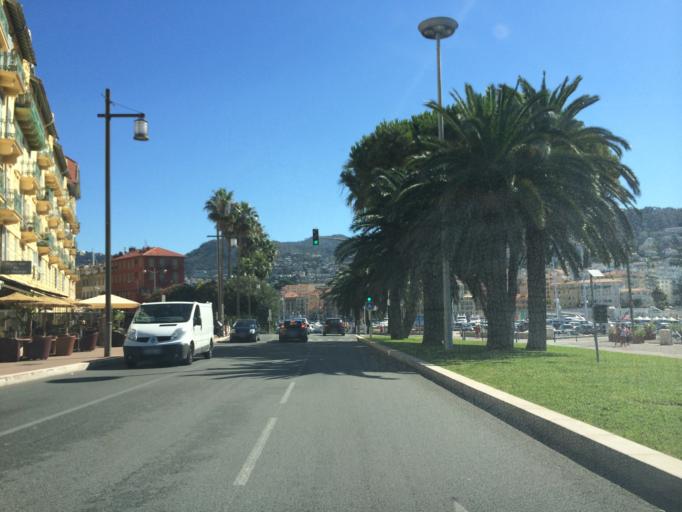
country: FR
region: Provence-Alpes-Cote d'Azur
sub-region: Departement des Alpes-Maritimes
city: Nice
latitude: 43.6934
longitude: 7.2818
